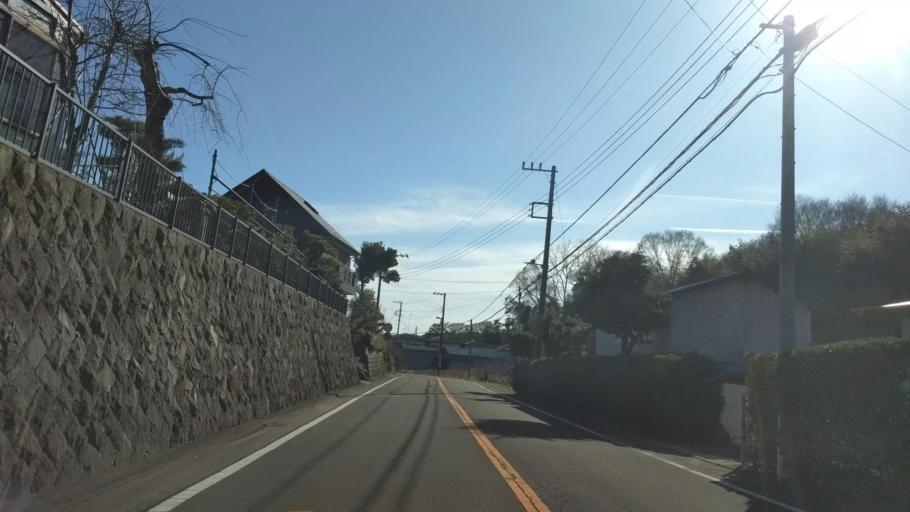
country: JP
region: Kanagawa
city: Ninomiya
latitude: 35.3344
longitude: 139.2327
